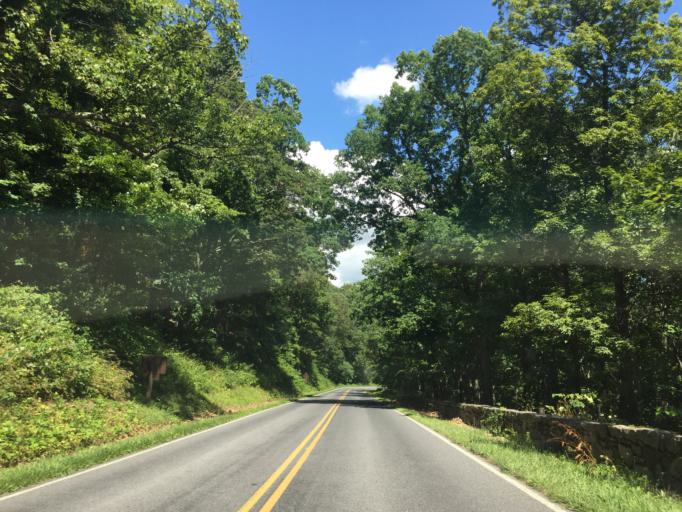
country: US
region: Virginia
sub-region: Warren County
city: Front Royal
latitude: 38.8365
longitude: -78.2026
